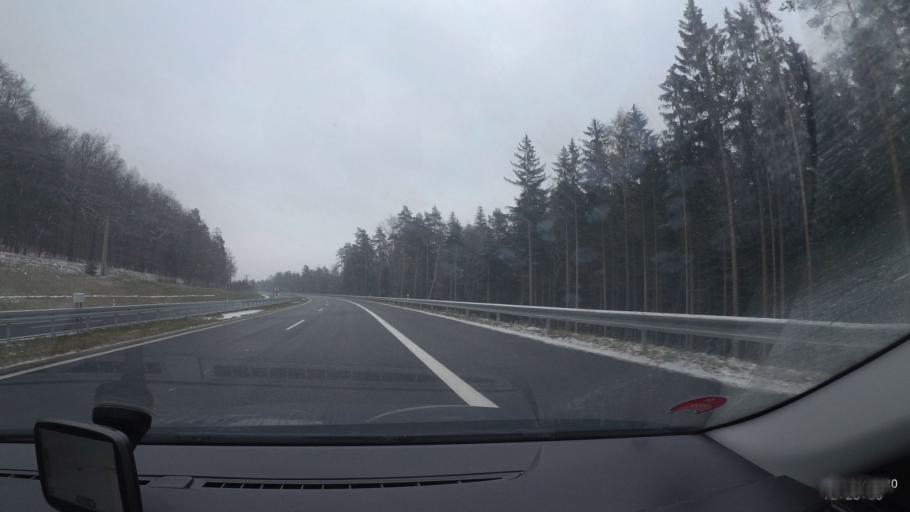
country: CZ
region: Central Bohemia
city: Nove Straseci
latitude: 50.1641
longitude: 13.8533
